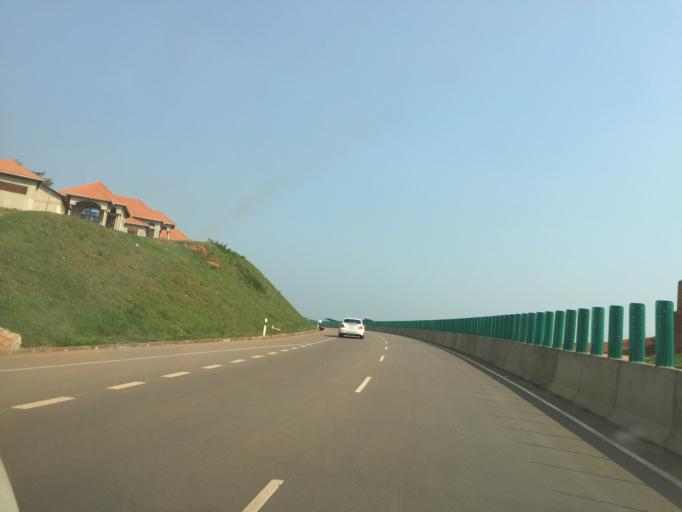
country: UG
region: Central Region
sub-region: Wakiso District
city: Kajansi
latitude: 0.2087
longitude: 32.5463
